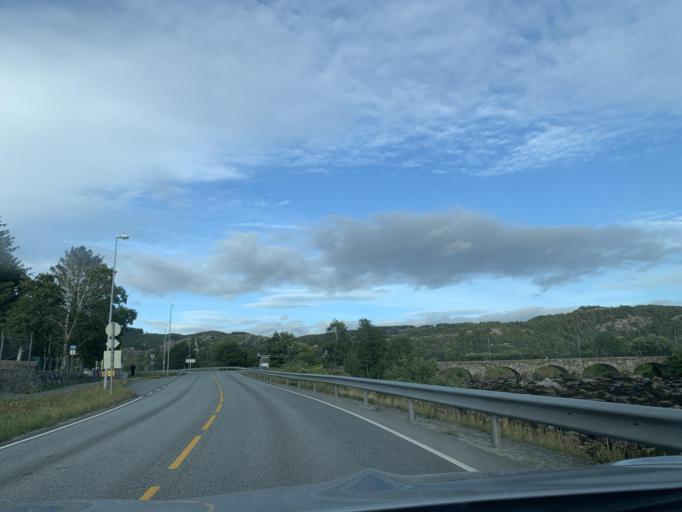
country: NO
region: Rogaland
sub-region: Eigersund
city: Egersund
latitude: 58.4604
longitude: 6.0132
